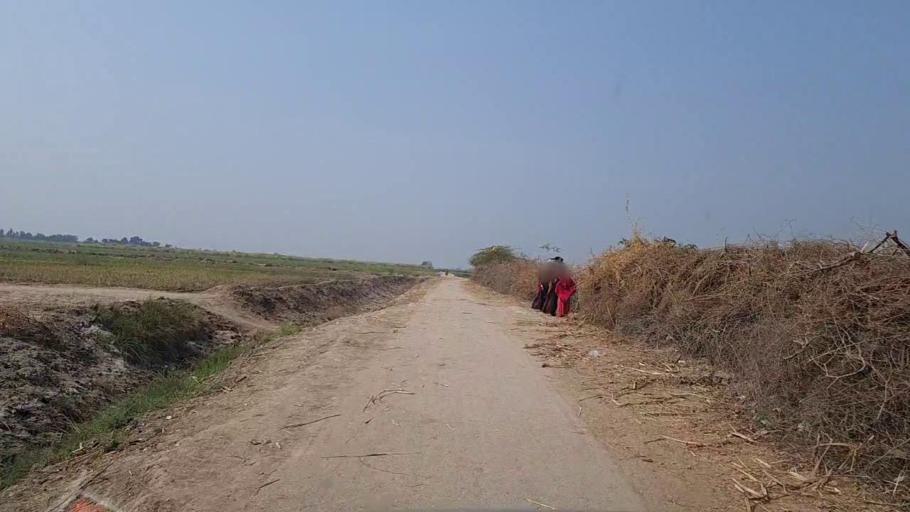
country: PK
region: Sindh
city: Mirwah Gorchani
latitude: 25.3359
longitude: 68.9887
